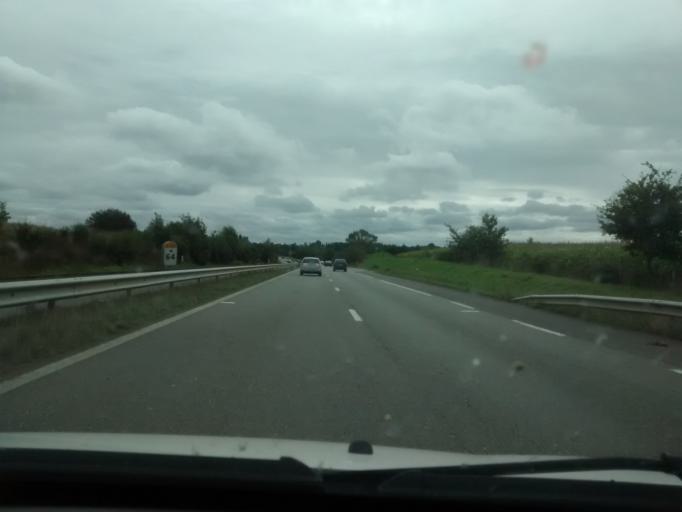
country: FR
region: Brittany
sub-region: Departement d'Ille-et-Vilaine
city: La Meziere
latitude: 48.2393
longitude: -1.7595
